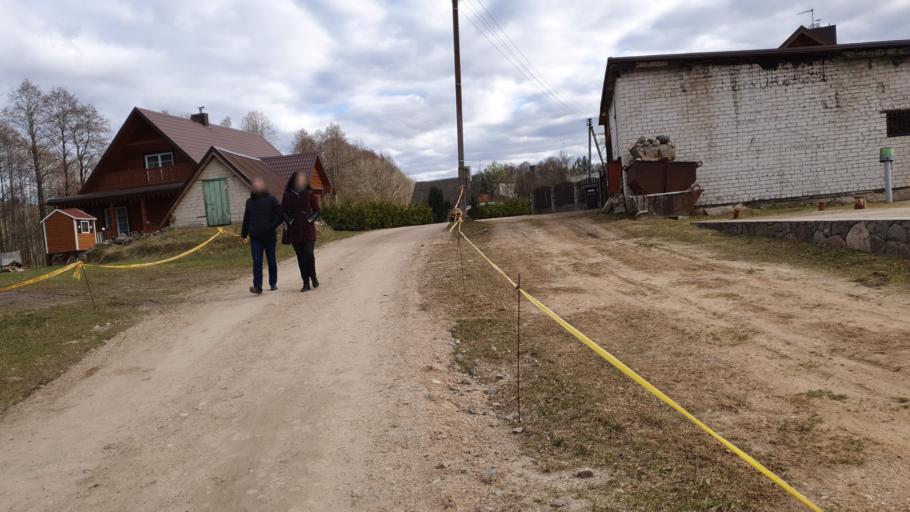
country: LT
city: Grigiskes
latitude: 54.7354
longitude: 25.0263
